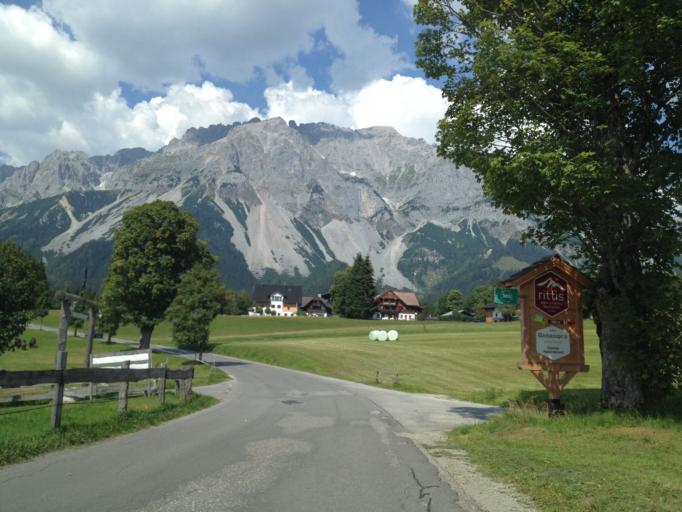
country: AT
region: Styria
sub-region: Politischer Bezirk Liezen
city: Schladming
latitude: 47.4158
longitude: 13.6380
